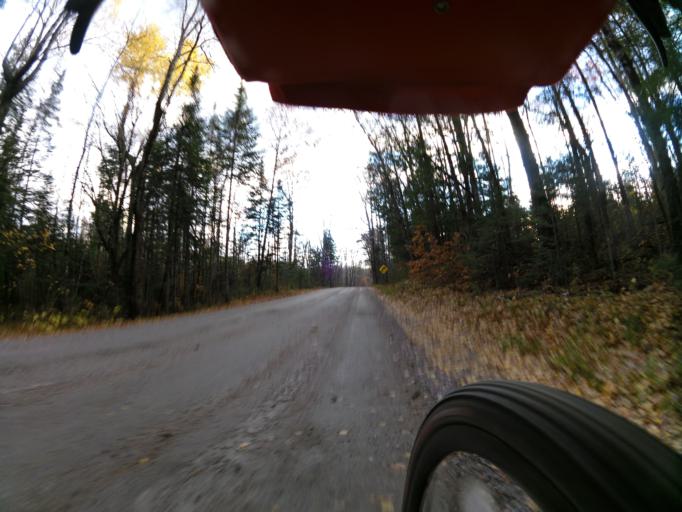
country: CA
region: Quebec
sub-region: Outaouais
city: Shawville
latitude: 45.6636
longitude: -76.3000
